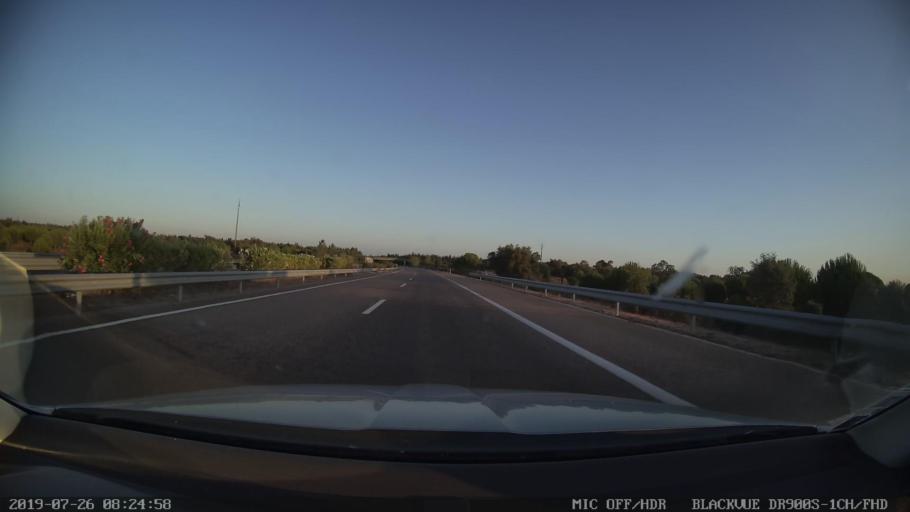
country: PT
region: Evora
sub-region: Vendas Novas
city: Vendas Novas
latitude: 38.6424
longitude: -8.6661
